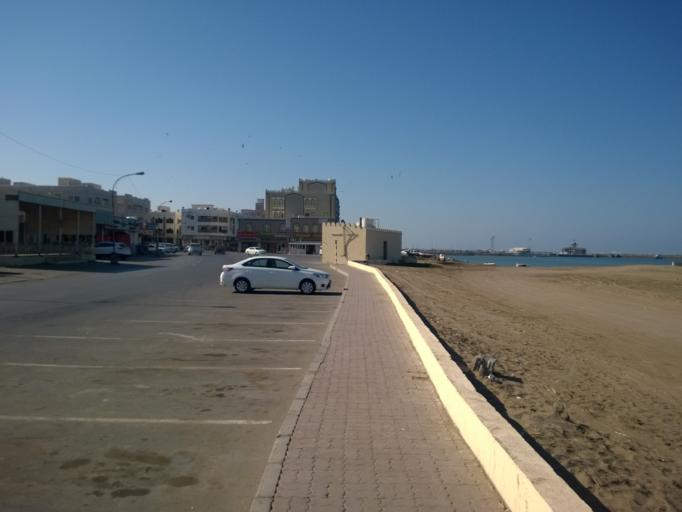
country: OM
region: Muhafazat Masqat
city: As Sib al Jadidah
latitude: 23.6853
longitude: 58.1842
